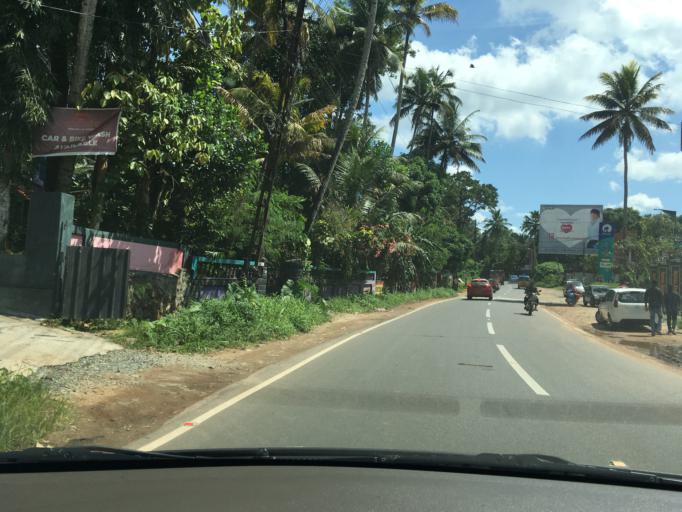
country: IN
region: Kerala
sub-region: Thiruvananthapuram
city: Nedumangad
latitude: 8.5988
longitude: 76.9955
